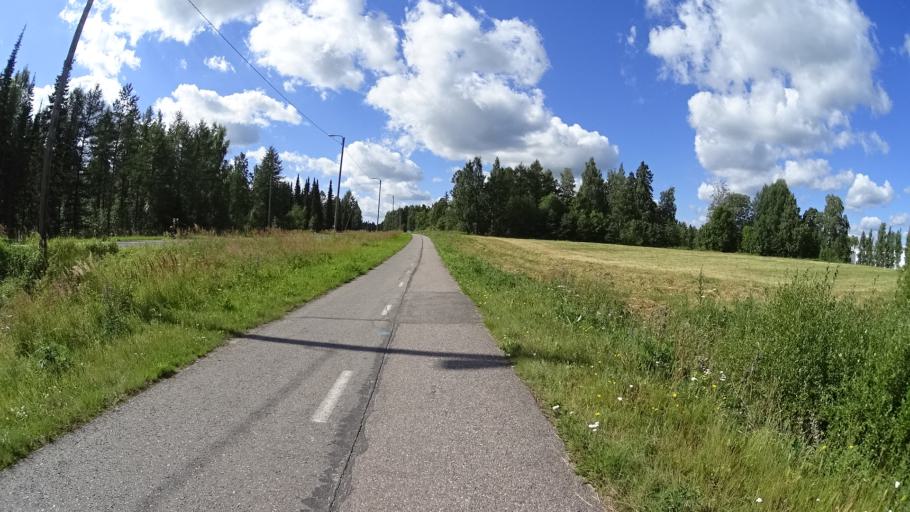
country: FI
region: Uusimaa
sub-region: Helsinki
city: Tuusula
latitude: 60.4326
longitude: 25.0589
